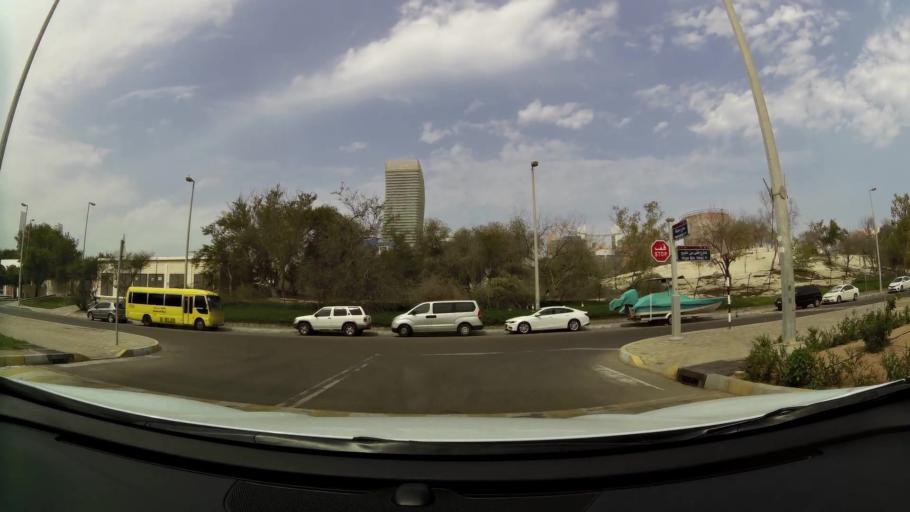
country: AE
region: Abu Dhabi
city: Abu Dhabi
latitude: 24.4653
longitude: 54.3439
